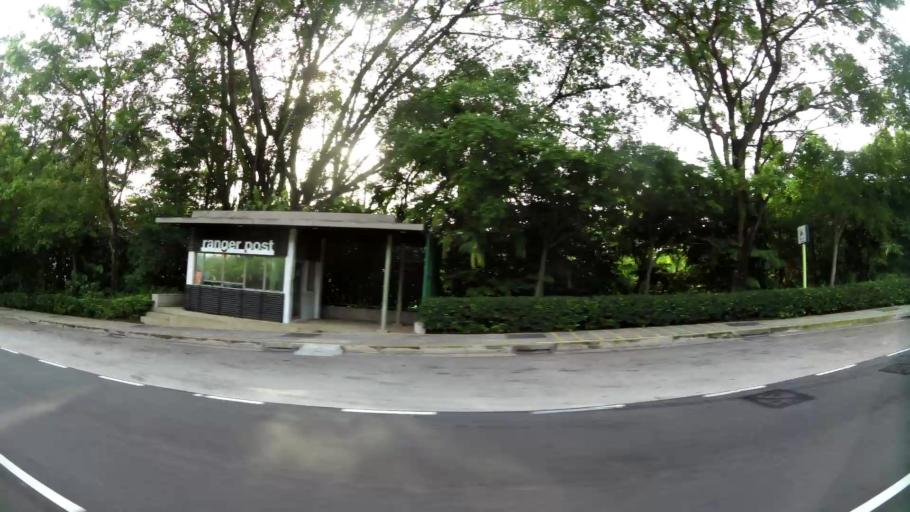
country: SG
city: Singapore
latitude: 1.2523
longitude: 103.8255
